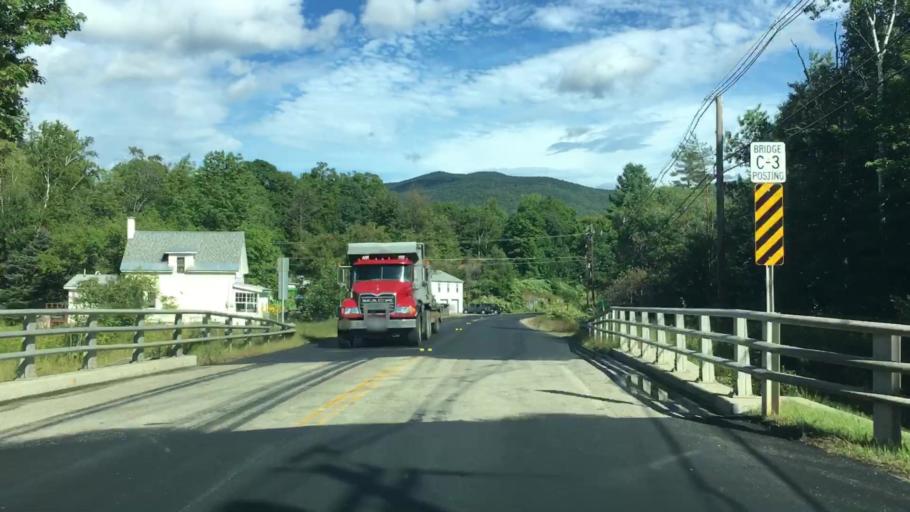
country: US
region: New Hampshire
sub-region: Grafton County
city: Woodstock
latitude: 44.0312
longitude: -71.6921
